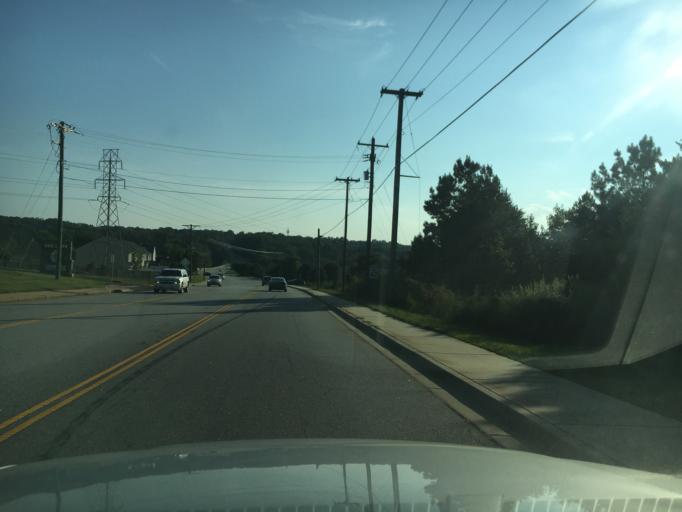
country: US
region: South Carolina
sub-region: Greenville County
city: Taylors
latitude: 34.9010
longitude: -82.2573
